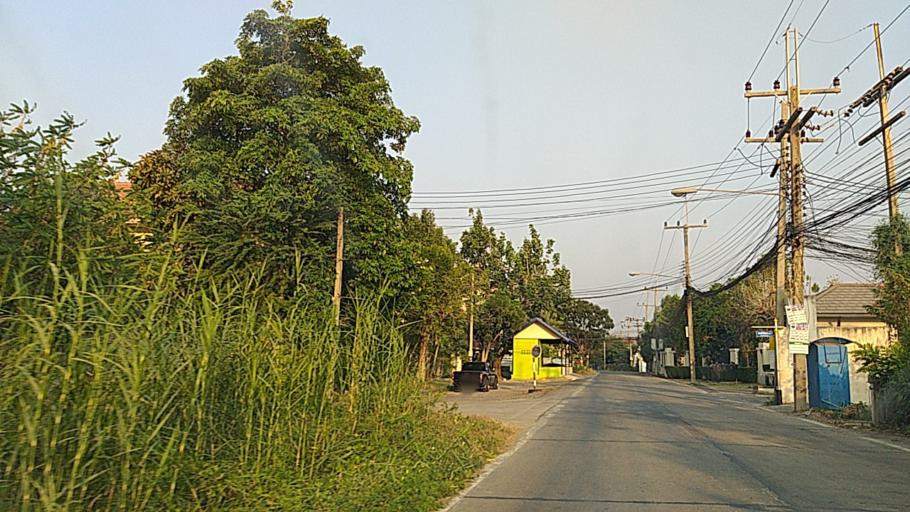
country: TH
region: Phra Nakhon Si Ayutthaya
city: Ban Bang Kadi Pathum Thani
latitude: 13.9947
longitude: 100.5618
